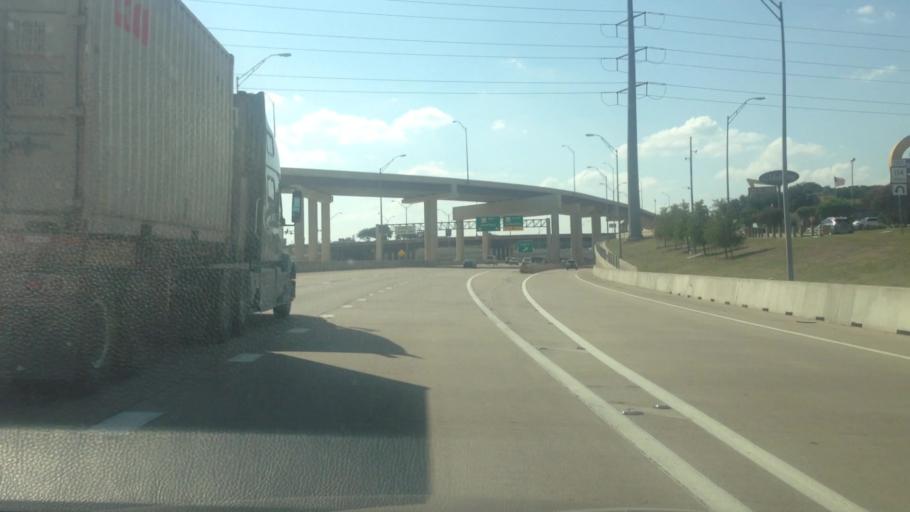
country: US
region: Texas
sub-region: Tarrant County
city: Grapevine
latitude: 32.9242
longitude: -97.0851
